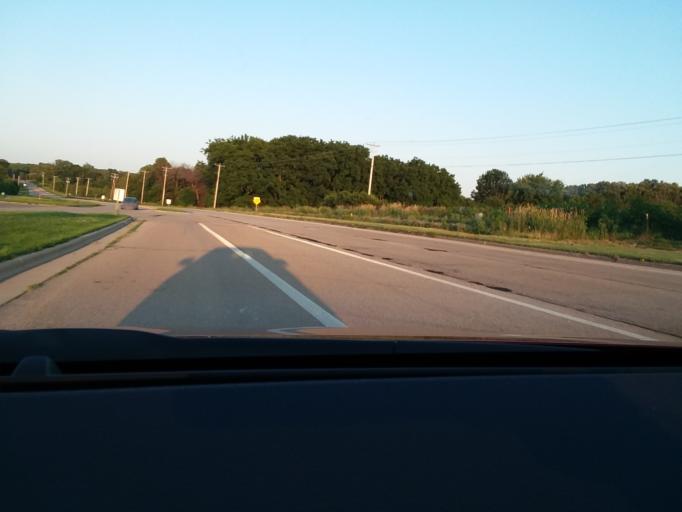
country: US
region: Wisconsin
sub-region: Dane County
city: Sun Prairie
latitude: 43.1435
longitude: -89.2794
